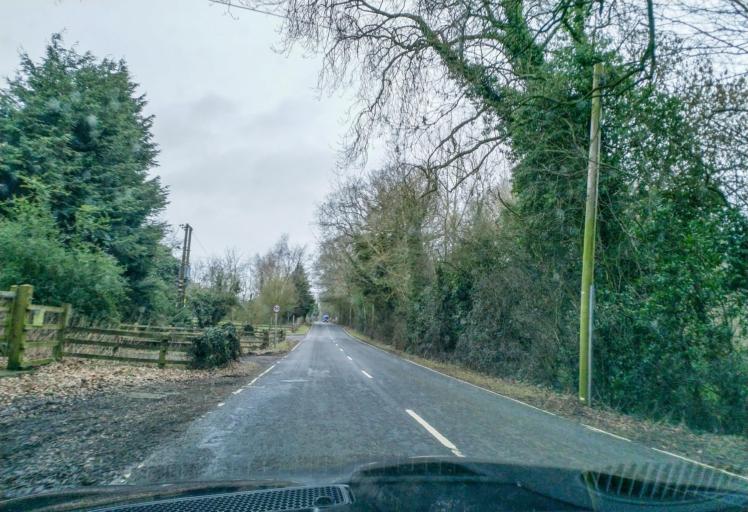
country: GB
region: England
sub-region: Warwickshire
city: Wroxall
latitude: 52.3178
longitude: -1.6729
